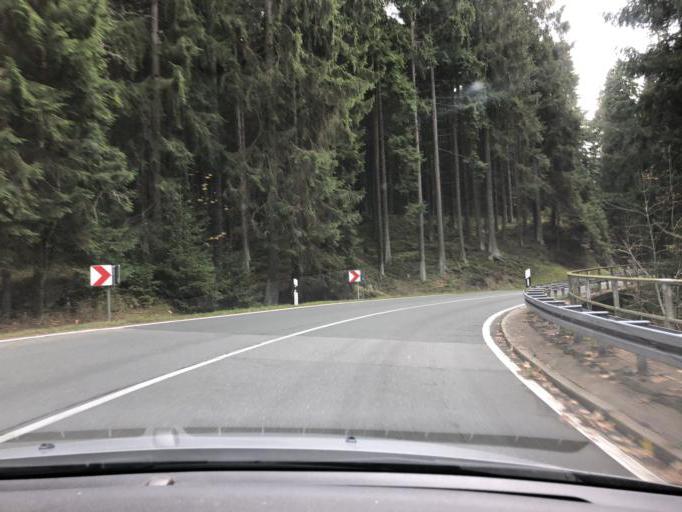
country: DE
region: Thuringia
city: Neuhaus am Rennweg
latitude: 50.5314
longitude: 11.1253
